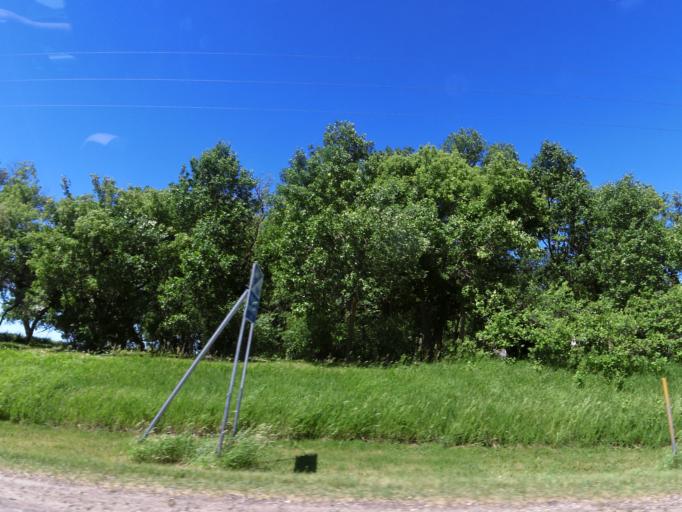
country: US
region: Minnesota
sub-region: Mahnomen County
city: Mahnomen
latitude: 47.1707
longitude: -95.9331
